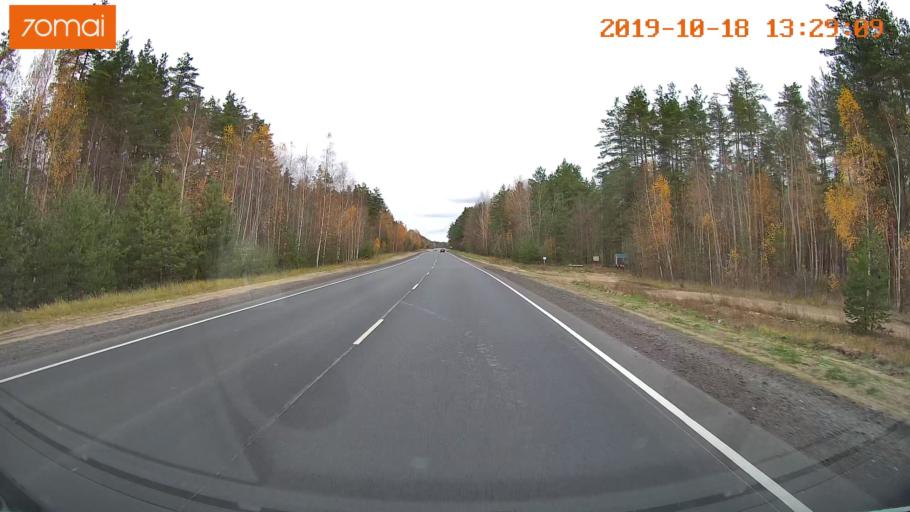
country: RU
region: Rjazan
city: Solotcha
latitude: 54.7899
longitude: 39.8728
